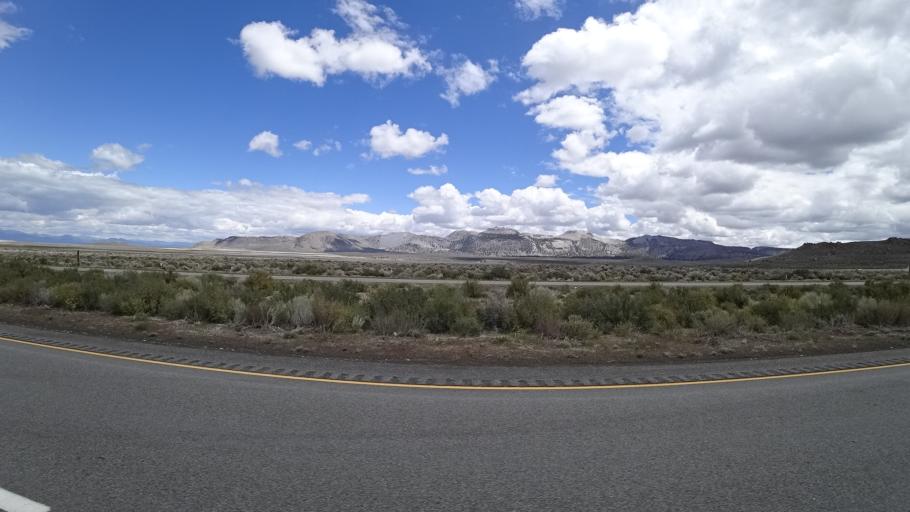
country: US
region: California
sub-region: Mono County
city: Mammoth Lakes
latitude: 37.8735
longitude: -119.0888
